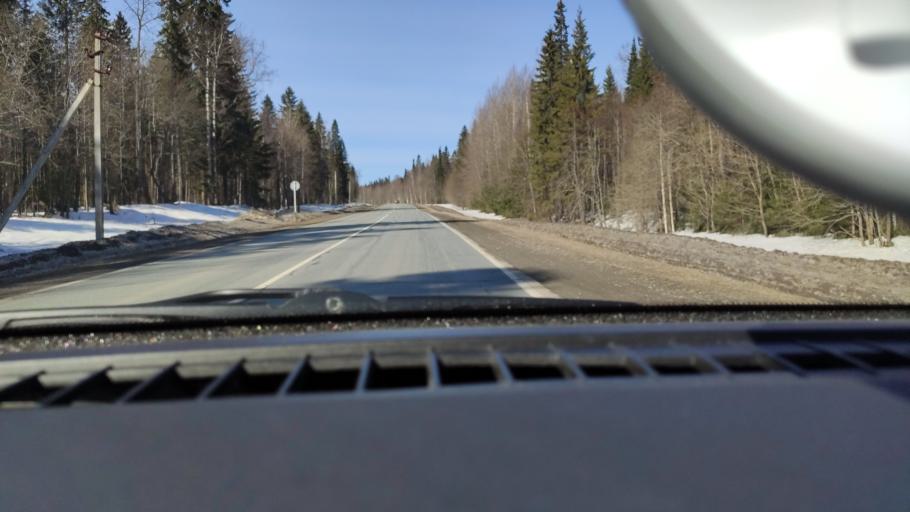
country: RU
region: Perm
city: Perm
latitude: 58.2037
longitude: 56.2013
